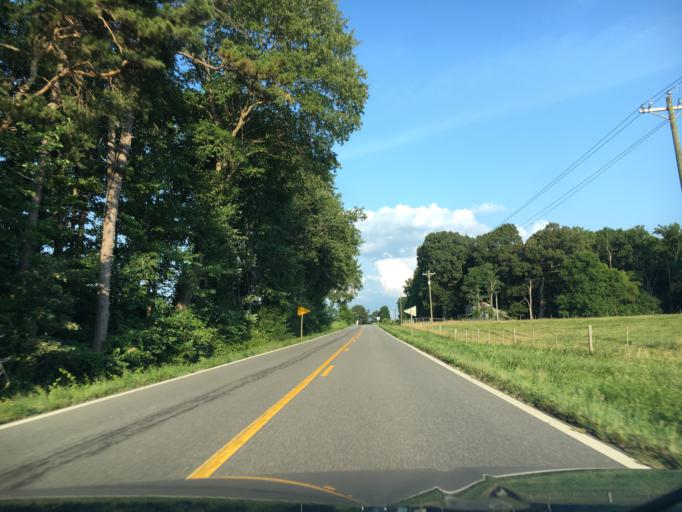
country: US
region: Virginia
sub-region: Halifax County
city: Mountain Road
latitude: 36.8305
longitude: -79.1158
